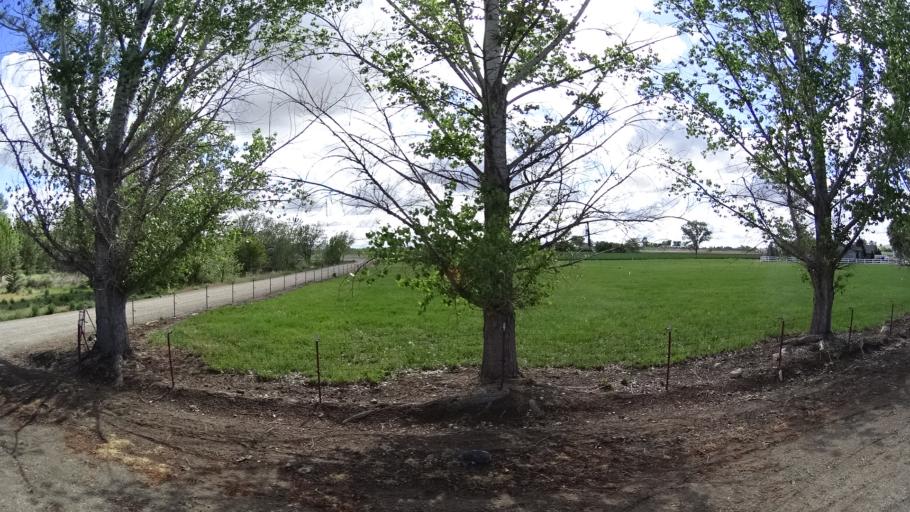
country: US
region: Idaho
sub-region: Ada County
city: Kuna
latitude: 43.4960
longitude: -116.4735
